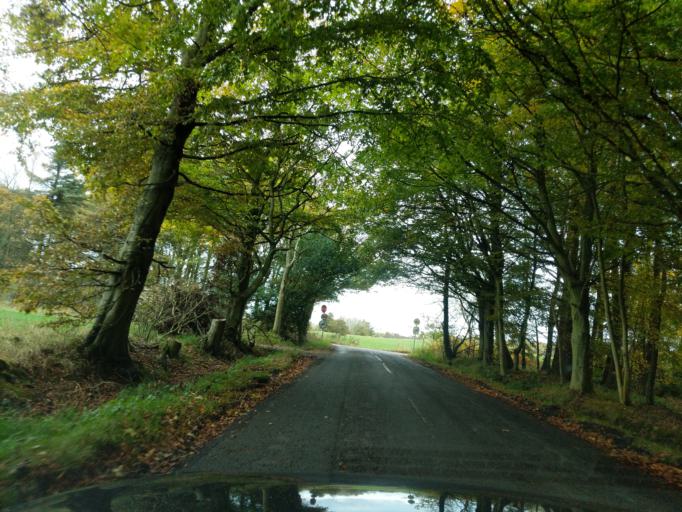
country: GB
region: Scotland
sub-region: Fife
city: Saint Andrews
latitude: 56.2932
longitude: -2.7531
